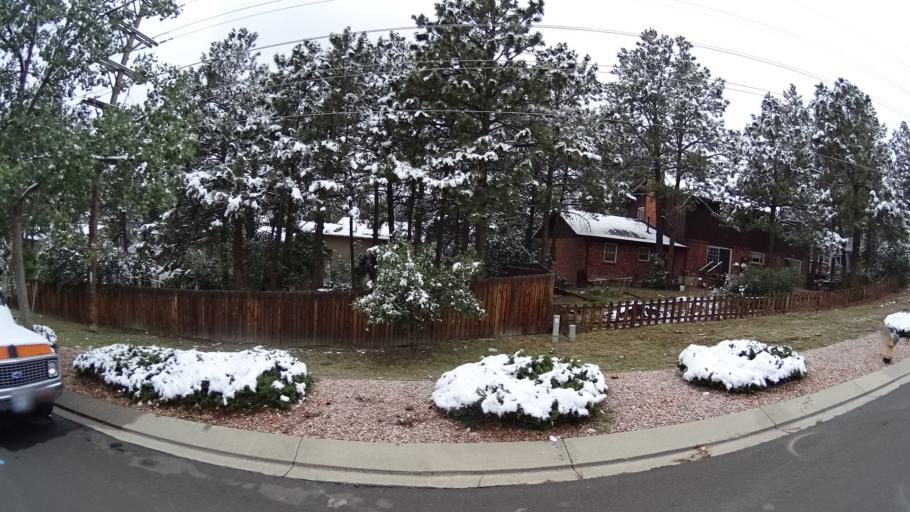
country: US
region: Colorado
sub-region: El Paso County
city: Colorado Springs
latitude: 38.9185
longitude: -104.7936
